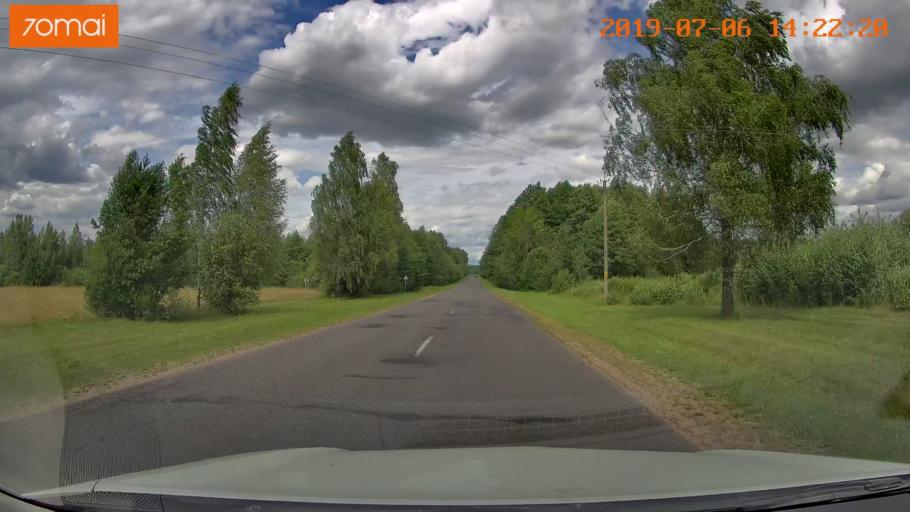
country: BY
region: Minsk
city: Ivyanyets
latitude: 53.9072
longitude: 26.7626
